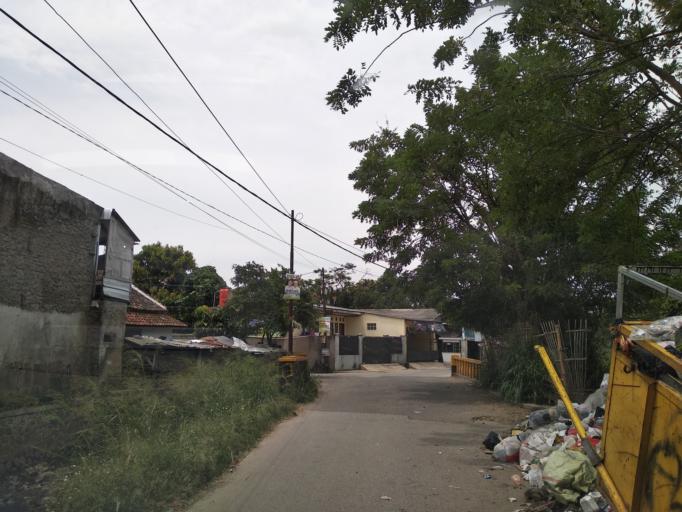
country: ID
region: West Java
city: Pameungpeuk
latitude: -6.9761
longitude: 107.6486
